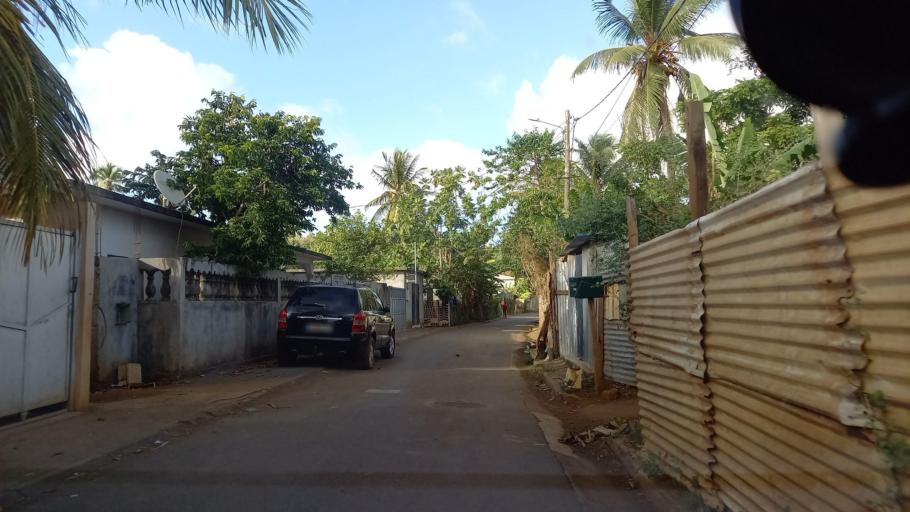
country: YT
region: Bandrele
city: Bandrele
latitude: -12.9121
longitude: 45.1949
